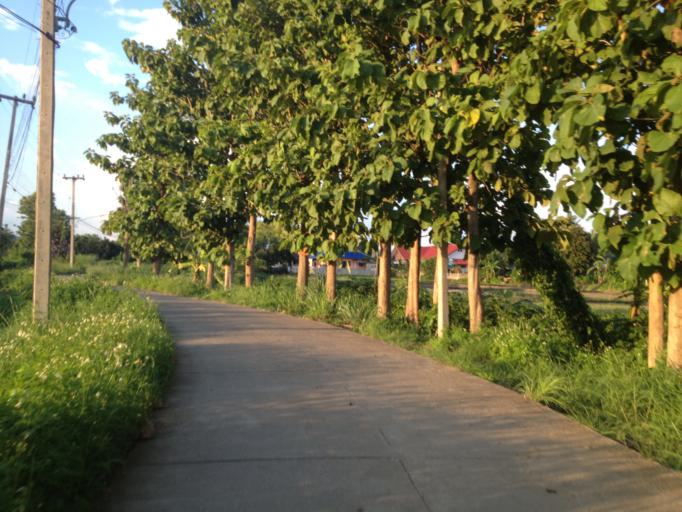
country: TH
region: Chiang Mai
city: Hang Dong
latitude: 18.6994
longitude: 98.9078
